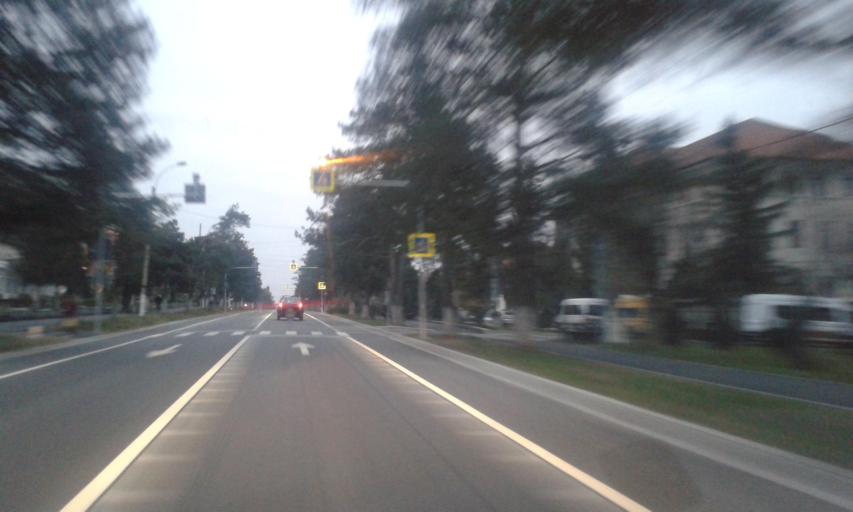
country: RO
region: Gorj
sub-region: Comuna Bumbesti-Jiu
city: Bumbesti-Jiu
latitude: 45.1801
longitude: 23.3797
